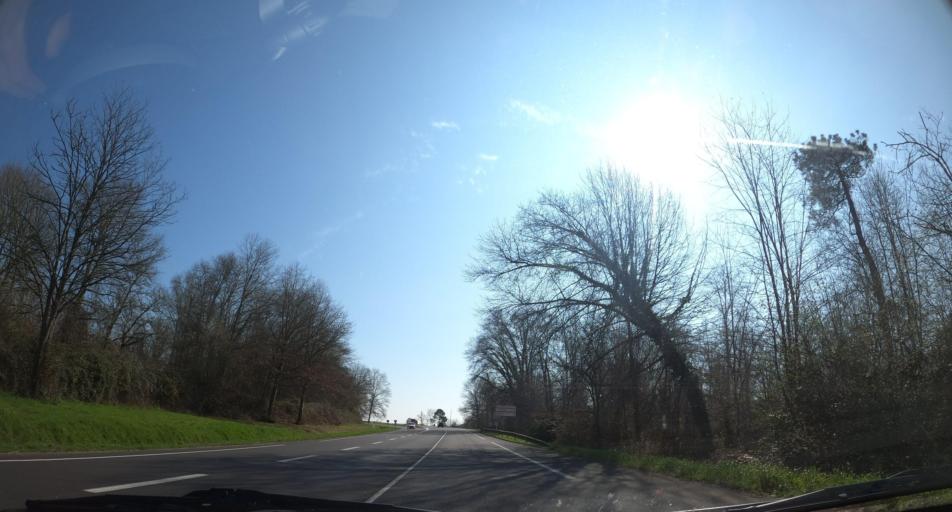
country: FR
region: Aquitaine
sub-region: Departement des Landes
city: Saint-Pierre-du-Mont
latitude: 43.8689
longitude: -0.5160
